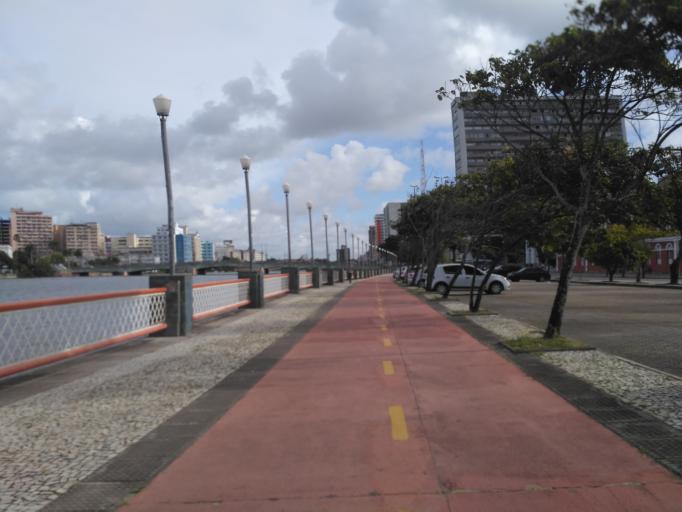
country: BR
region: Pernambuco
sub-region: Recife
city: Recife
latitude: -8.0576
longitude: -34.8783
